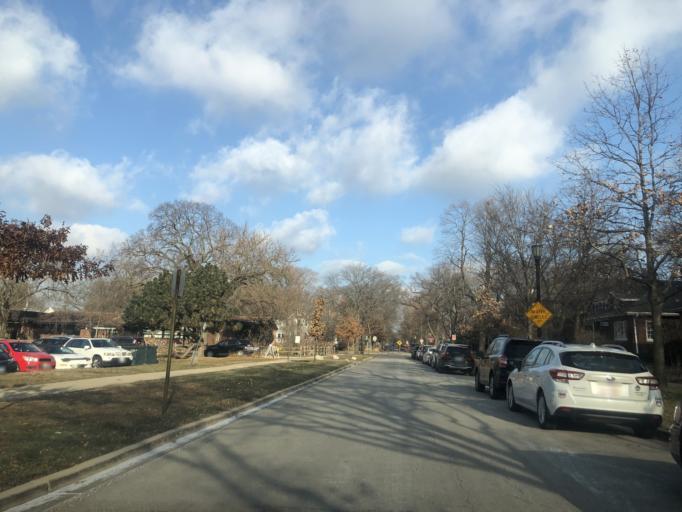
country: US
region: Illinois
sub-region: Cook County
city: Evanston
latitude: 42.0349
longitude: -87.6930
